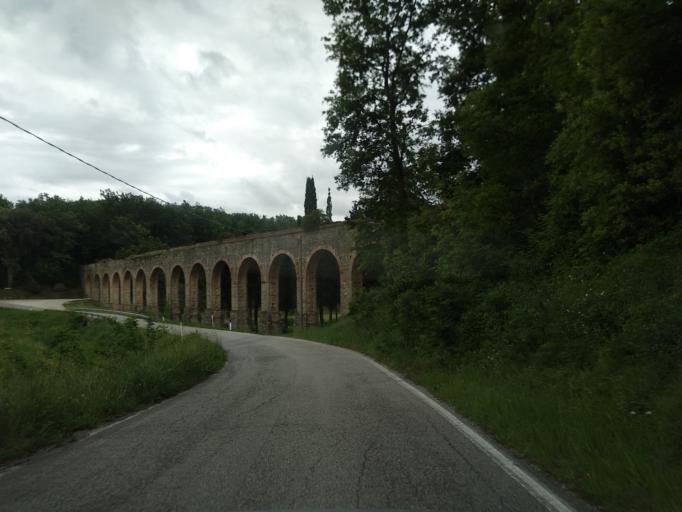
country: IT
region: Tuscany
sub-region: Provincia di Livorno
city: Guasticce
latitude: 43.5636
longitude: 10.4246
